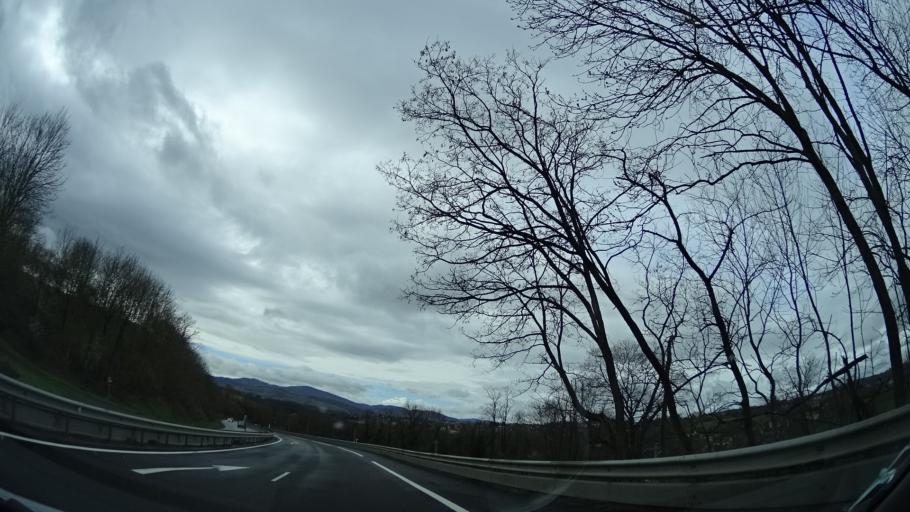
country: FR
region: Rhone-Alpes
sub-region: Departement du Rhone
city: Saint-Germain-Nuelles
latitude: 45.8396
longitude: 4.6335
